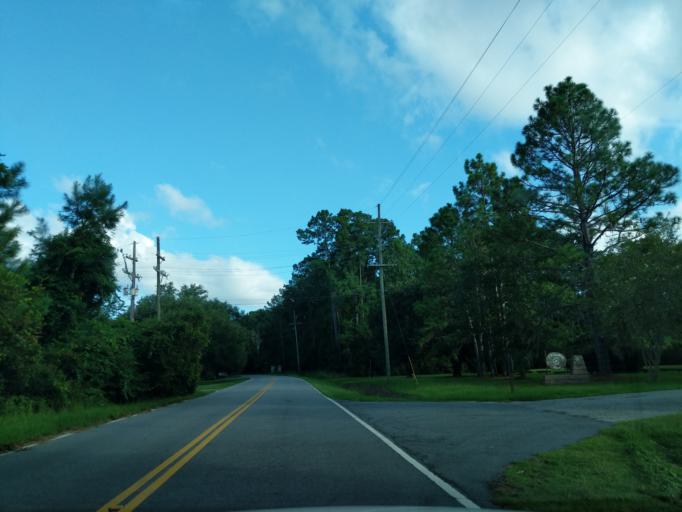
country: US
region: South Carolina
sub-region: Charleston County
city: Awendaw
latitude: 33.0981
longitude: -79.4679
